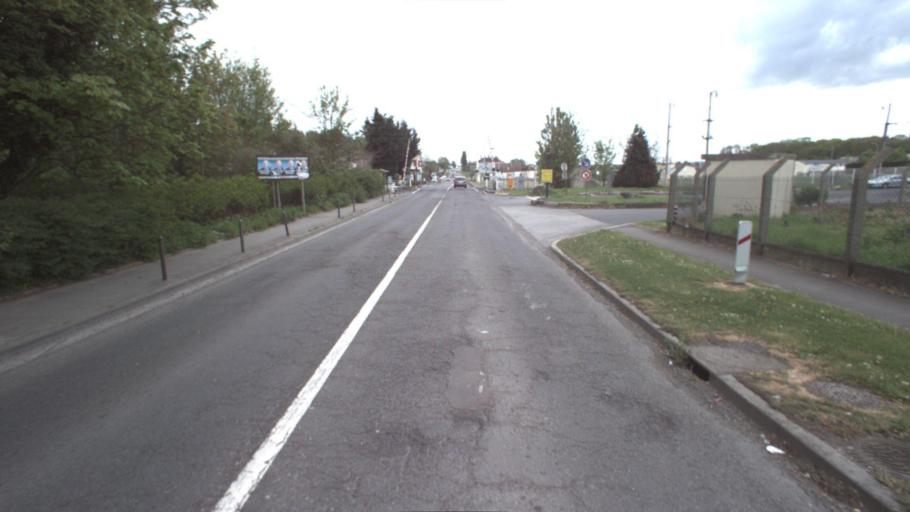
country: FR
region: Picardie
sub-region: Departement de l'Oise
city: Lagny-le-Sec
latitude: 49.0958
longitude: 2.7433
